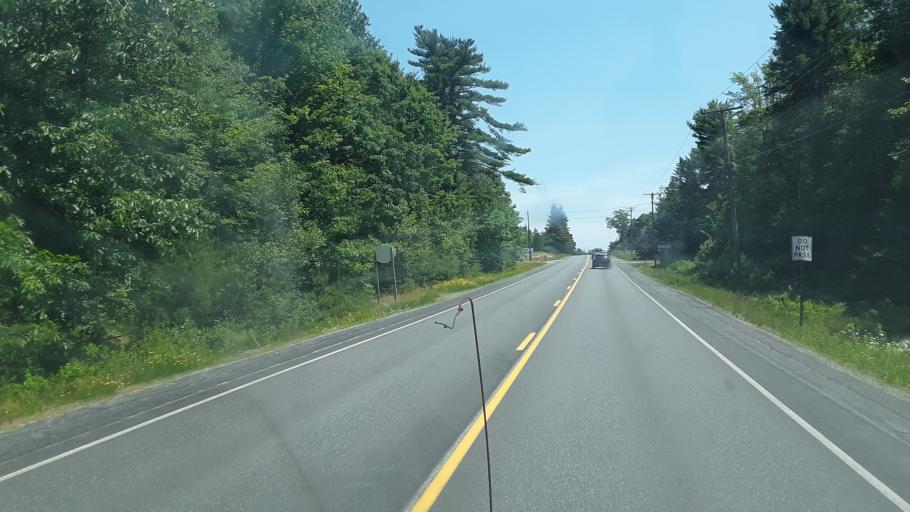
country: US
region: Maine
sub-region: Hancock County
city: Hancock
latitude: 44.5255
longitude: -68.2440
